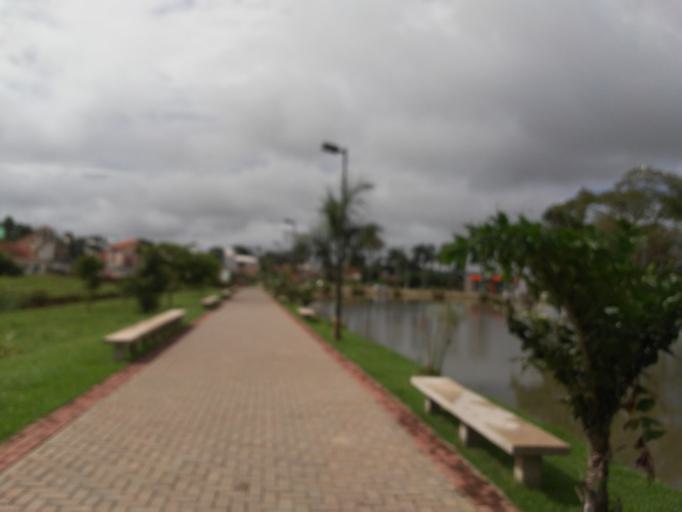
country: BR
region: Goias
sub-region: Ipameri
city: Ipameri
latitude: -17.7193
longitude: -48.1663
